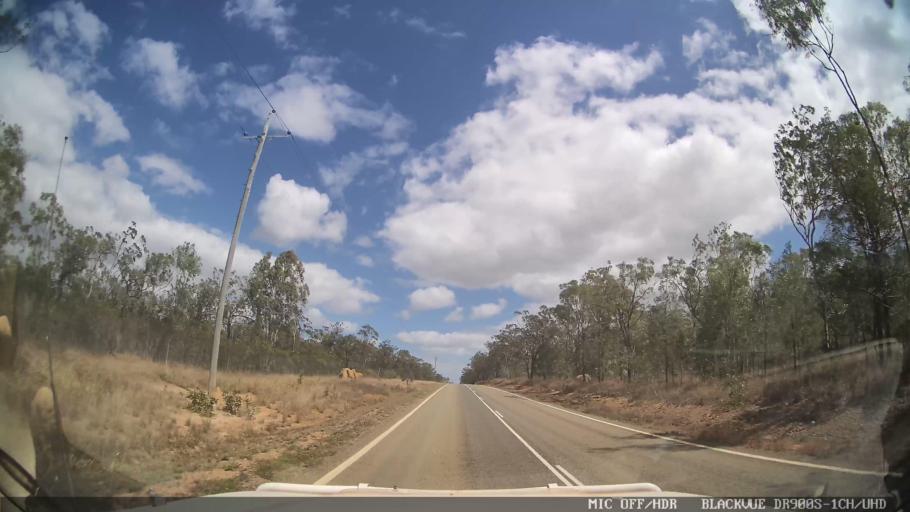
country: AU
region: Queensland
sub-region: Tablelands
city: Ravenshoe
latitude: -17.7242
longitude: 145.0506
